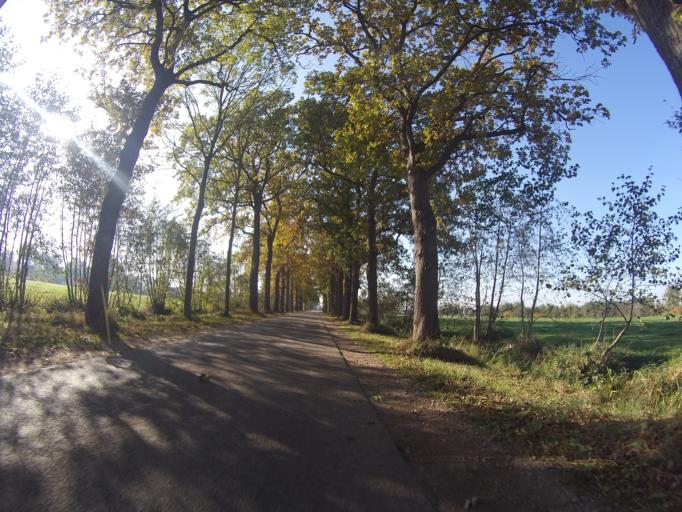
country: NL
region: Gelderland
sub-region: Gemeente Barneveld
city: Terschuur
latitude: 52.1775
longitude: 5.5383
